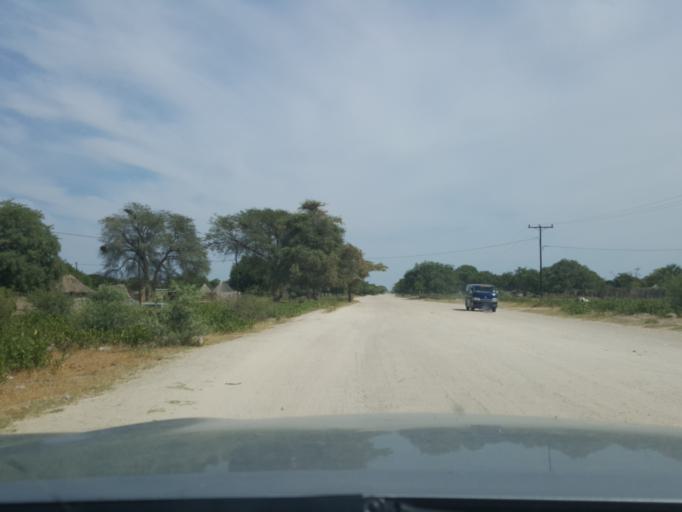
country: BW
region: North West
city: Shakawe
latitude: -18.3133
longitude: 21.8985
